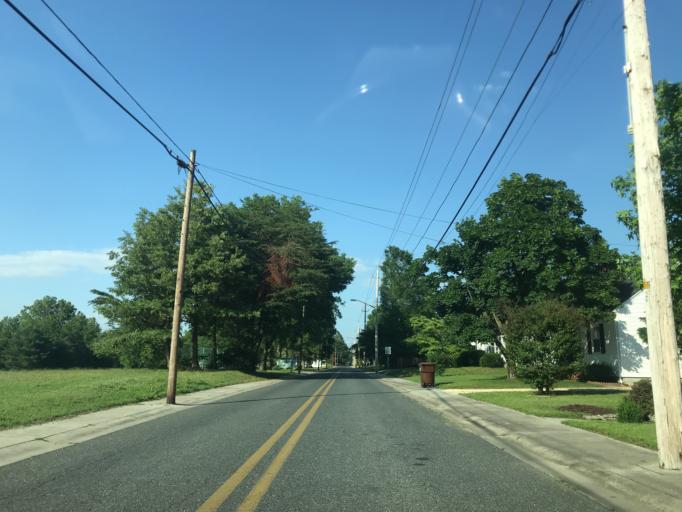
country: US
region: Maryland
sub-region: Wicomico County
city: Hebron
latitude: 38.5358
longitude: -75.7229
